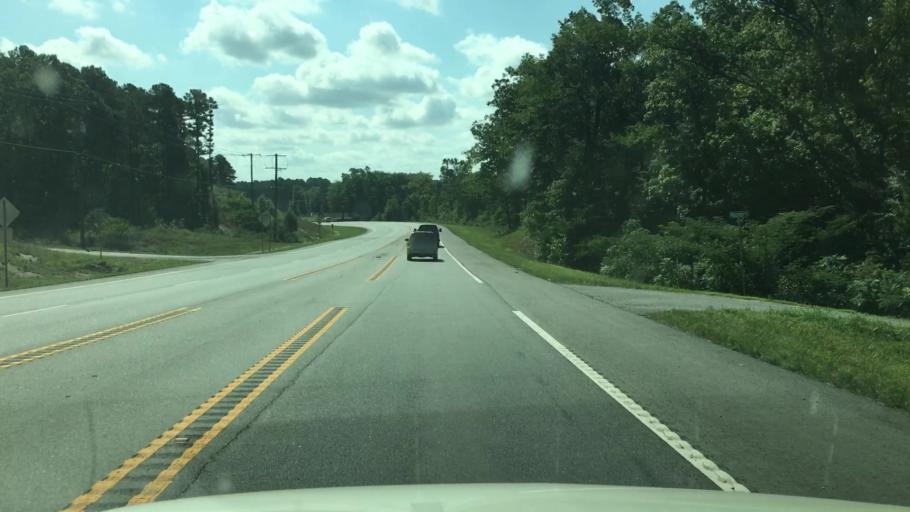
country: US
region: Arkansas
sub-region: Garland County
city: Piney
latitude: 34.5090
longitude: -93.1920
